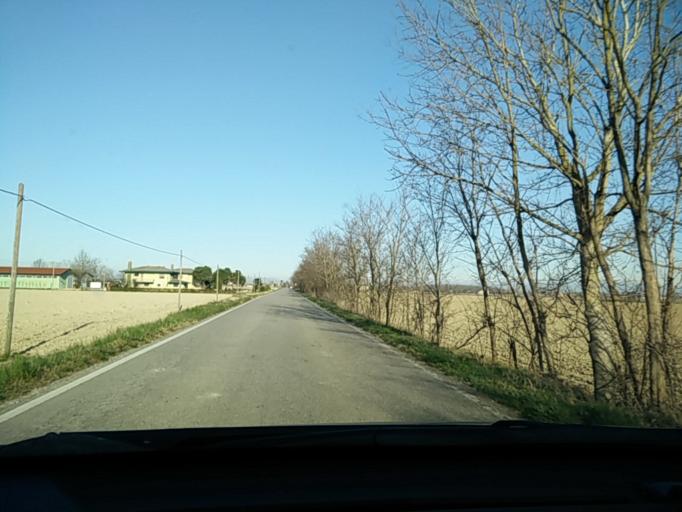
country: IT
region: Veneto
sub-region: Provincia di Venezia
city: Passarella
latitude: 45.5744
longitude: 12.6252
